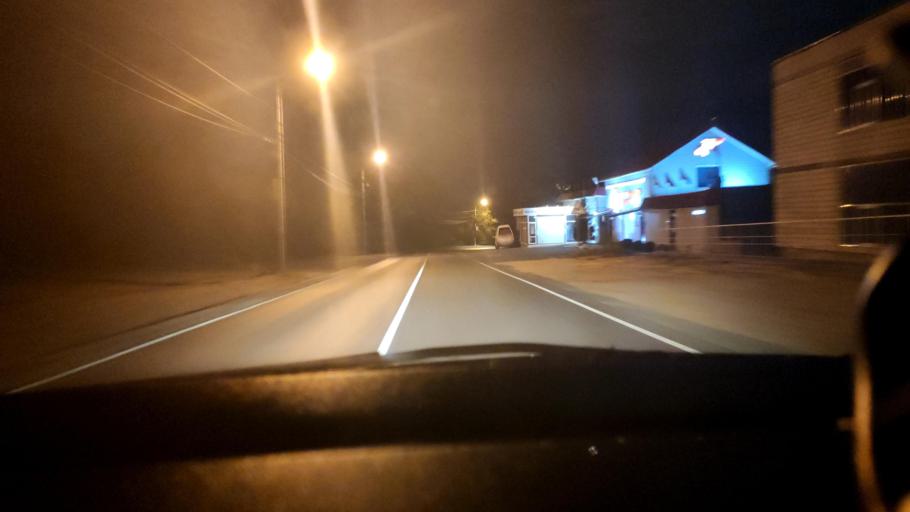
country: RU
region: Voronezj
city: Pridonskoy
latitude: 51.6465
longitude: 39.0981
